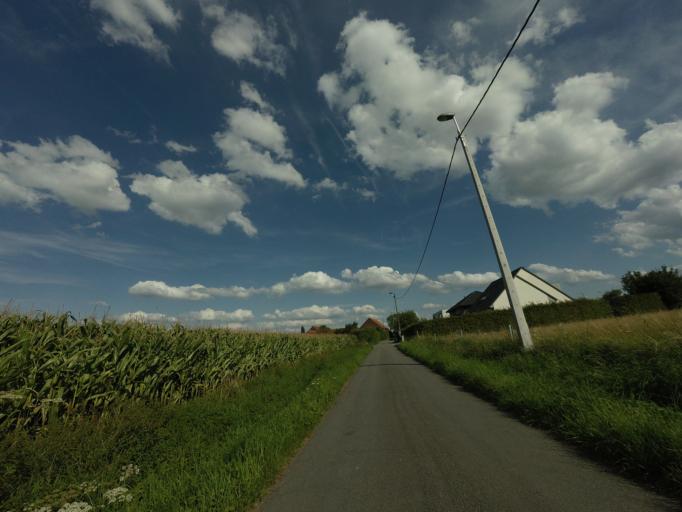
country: BE
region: Flanders
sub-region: Provincie Vlaams-Brabant
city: Meise
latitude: 50.9500
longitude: 4.3419
